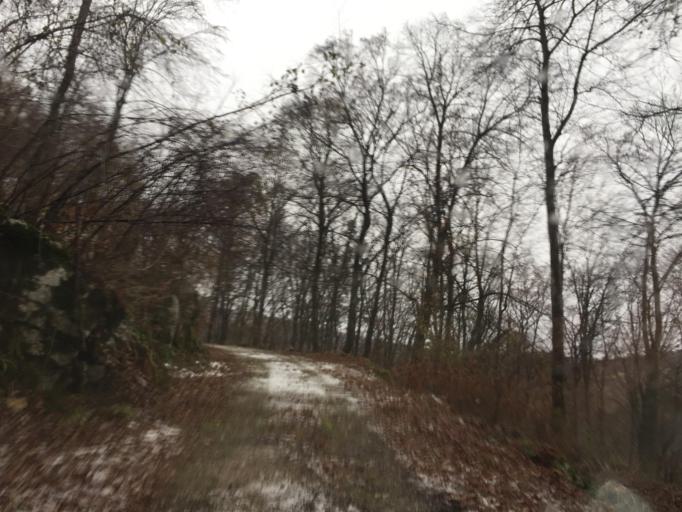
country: SI
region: Kanal
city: Kanal
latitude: 46.0673
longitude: 13.6694
